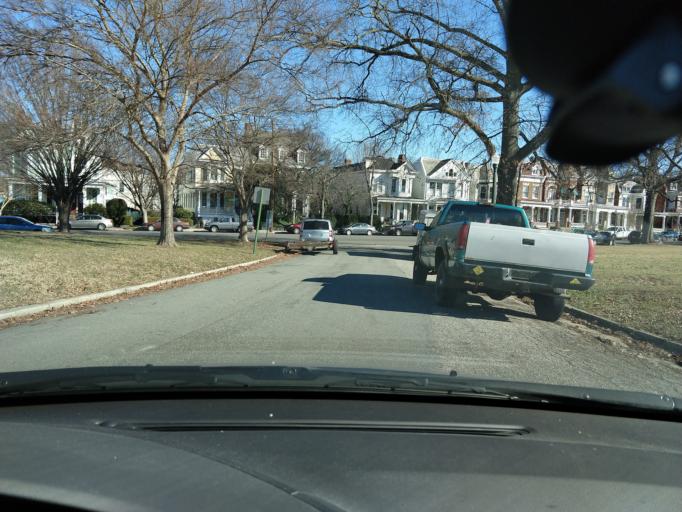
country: US
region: Virginia
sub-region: Henrico County
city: Montrose
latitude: 37.5263
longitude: -77.4108
